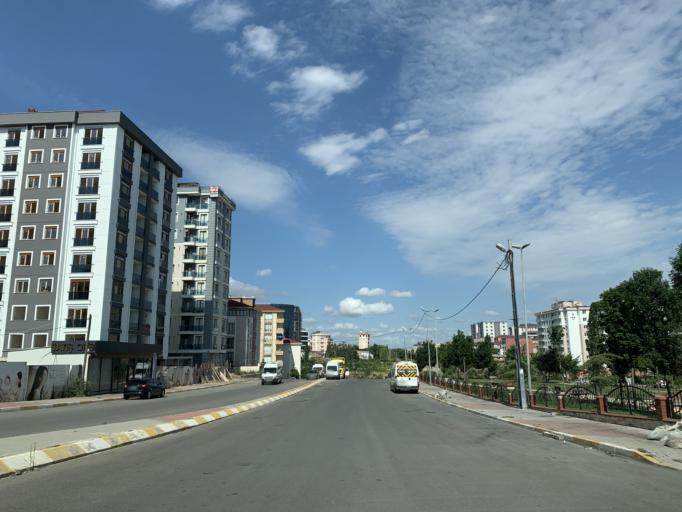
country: TR
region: Istanbul
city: Pendik
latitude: 40.8900
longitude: 29.2725
